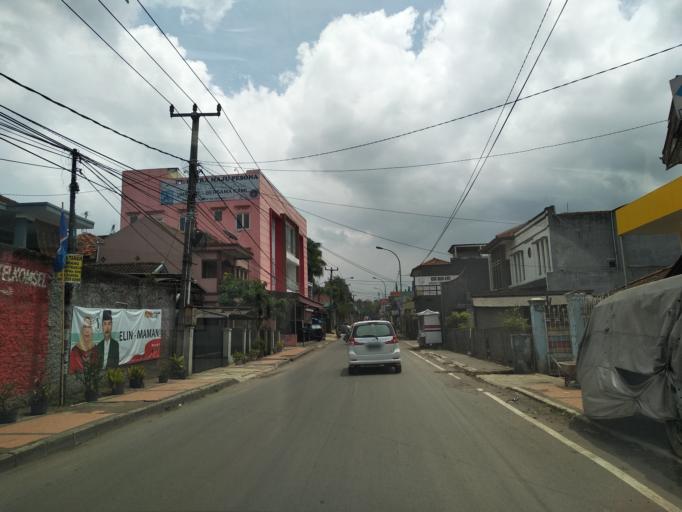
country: ID
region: West Java
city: Lembang
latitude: -6.8163
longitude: 107.6172
